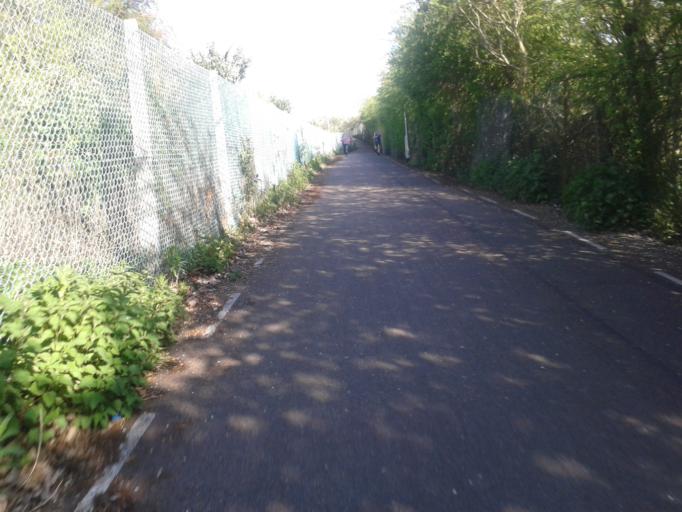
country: GB
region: England
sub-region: Cambridgeshire
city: Cambridge
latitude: 52.1954
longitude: 0.1615
